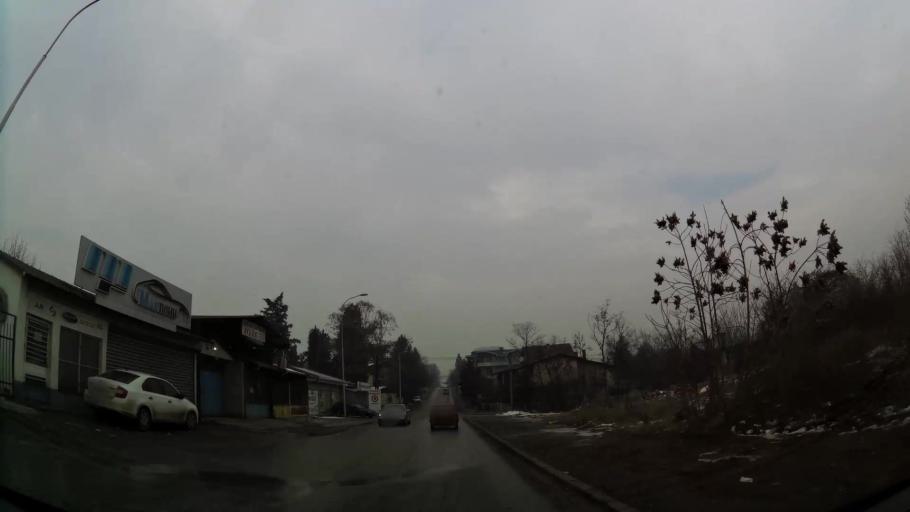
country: MK
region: Cair
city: Cair
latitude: 42.0173
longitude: 21.4534
